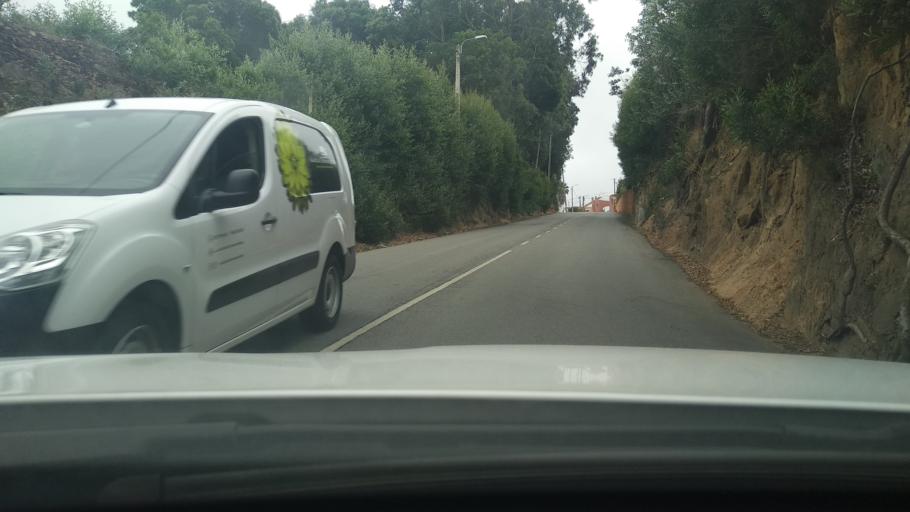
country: PT
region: Aveiro
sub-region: Espinho
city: Silvalde
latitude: 40.9962
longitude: -8.6268
